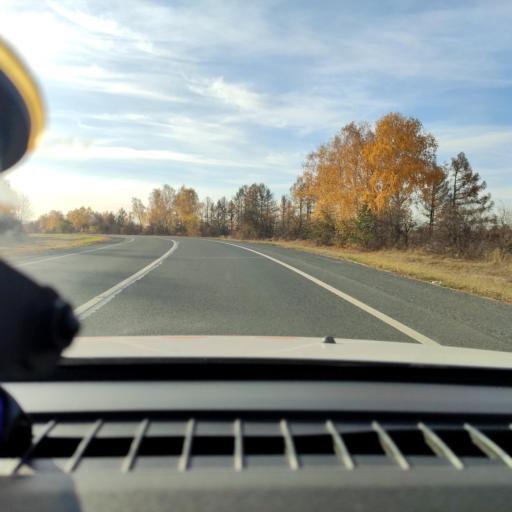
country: RU
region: Samara
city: Bereza
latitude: 53.4777
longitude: 50.1165
